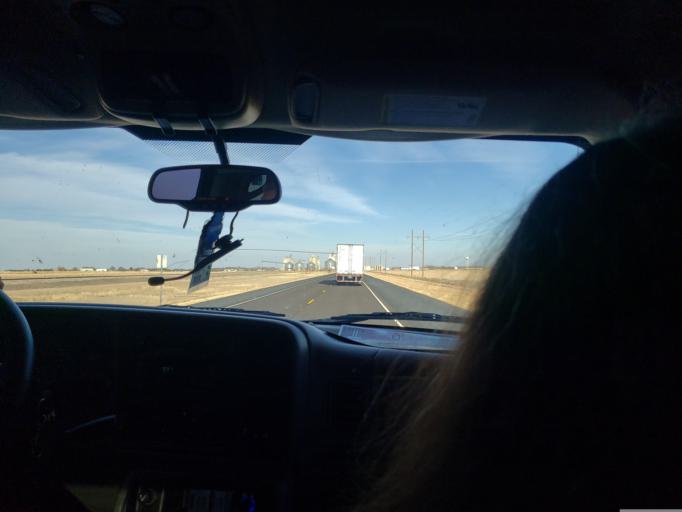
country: US
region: Oklahoma
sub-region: Texas County
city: Goodwell
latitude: 36.4899
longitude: -101.8043
